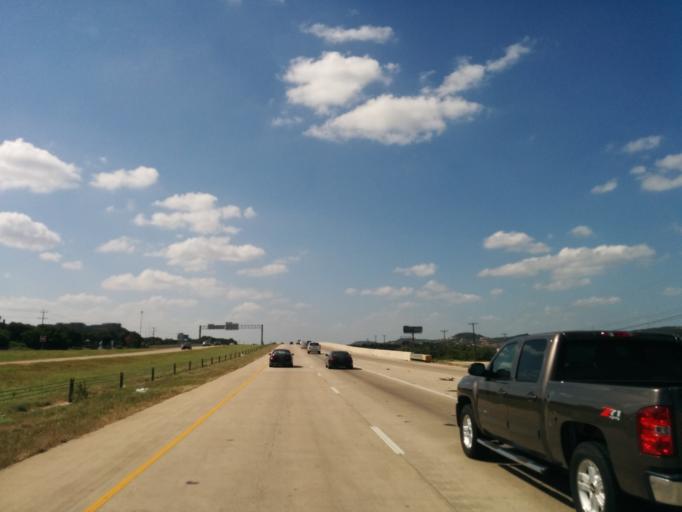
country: US
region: Texas
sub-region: Bexar County
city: Cross Mountain
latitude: 29.6217
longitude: -98.6084
